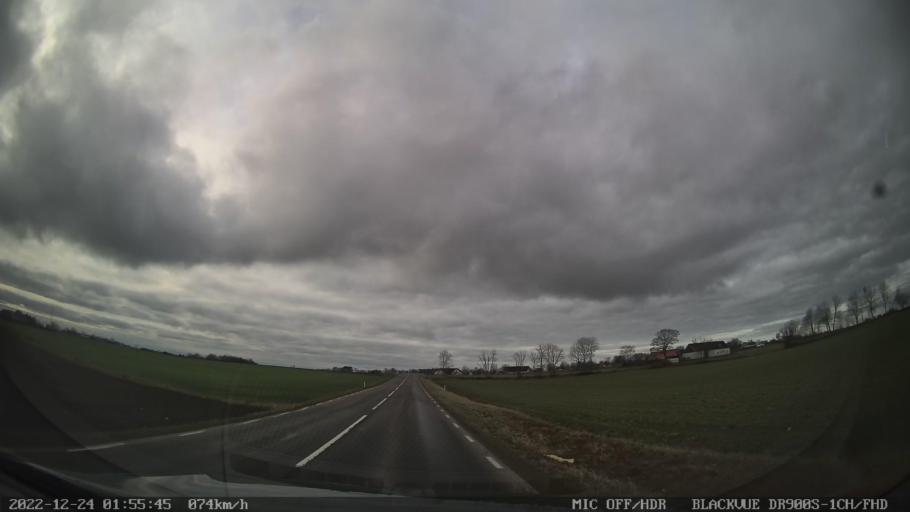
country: SE
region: Skane
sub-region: Tomelilla Kommun
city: Tomelilla
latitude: 55.5998
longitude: 14.0700
